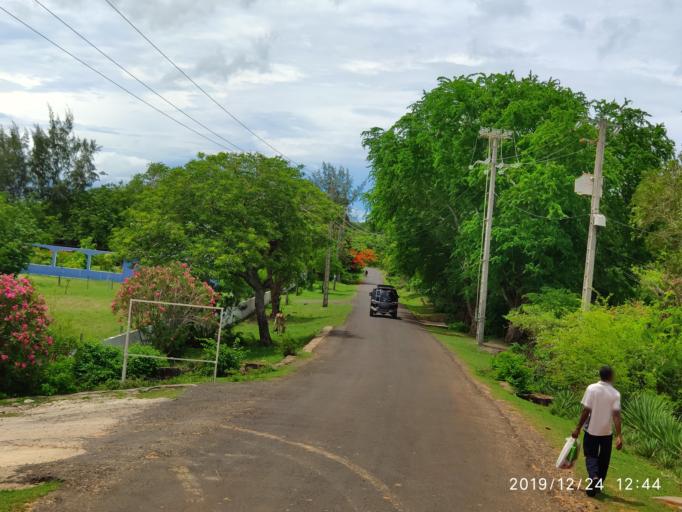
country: MG
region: Diana
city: Antsiranana
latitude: -12.2750
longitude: 49.3557
